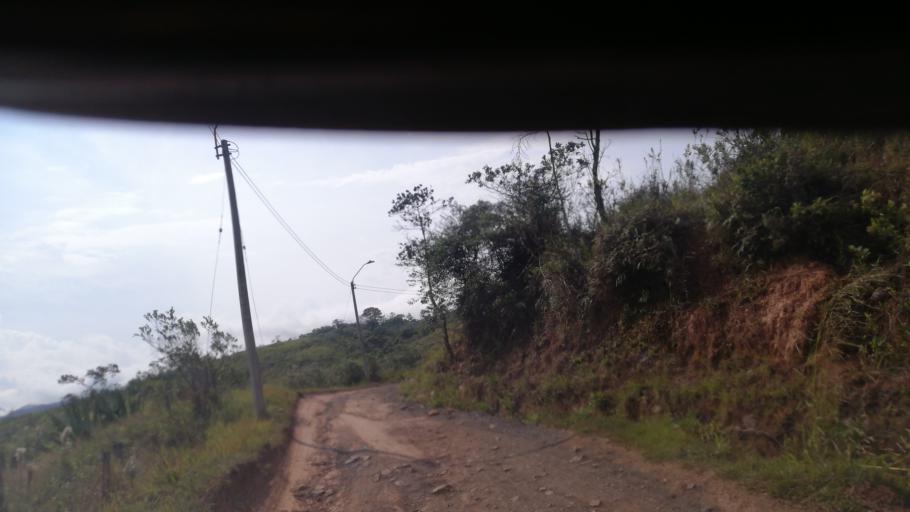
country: CO
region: Valle del Cauca
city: Cali
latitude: 3.4925
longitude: -76.5435
